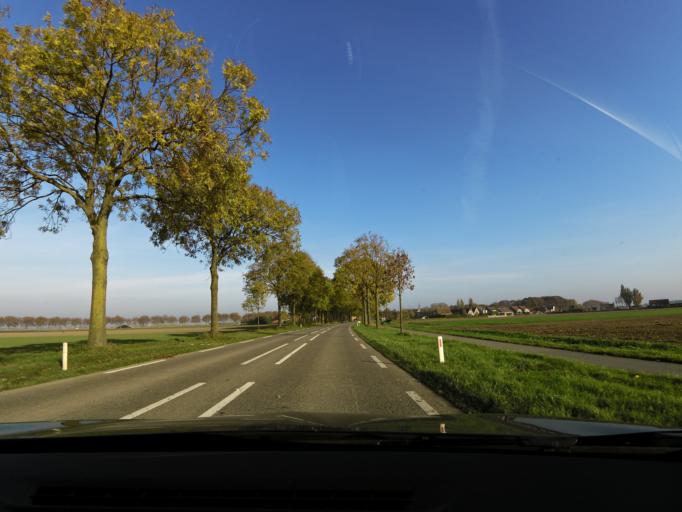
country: NL
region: North Brabant
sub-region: Gemeente Moerdijk
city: Klundert
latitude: 51.6487
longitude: 4.6558
